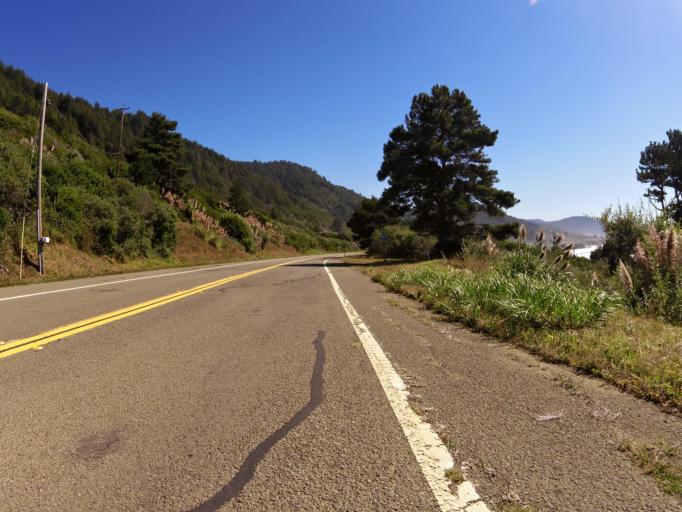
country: US
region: California
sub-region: Mendocino County
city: Fort Bragg
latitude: 39.6926
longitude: -123.7960
